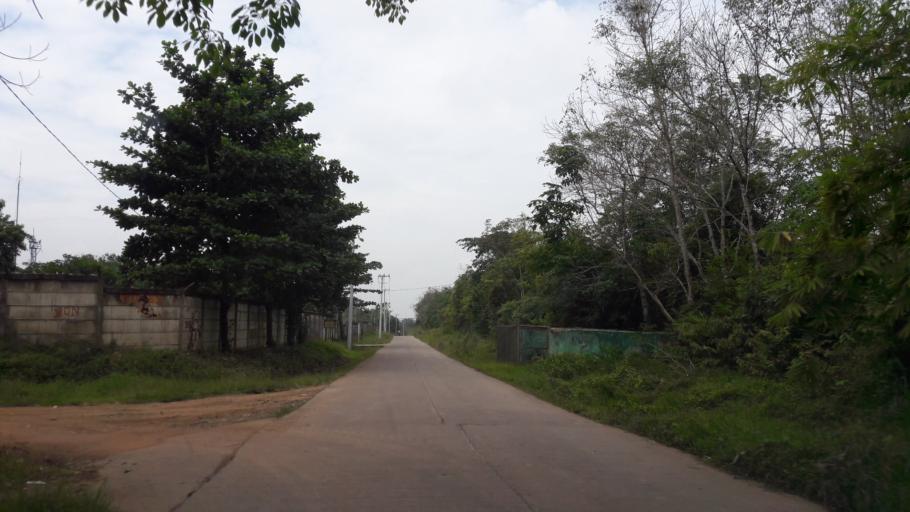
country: ID
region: South Sumatra
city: Gunungmenang
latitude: -3.2501
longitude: 104.1410
